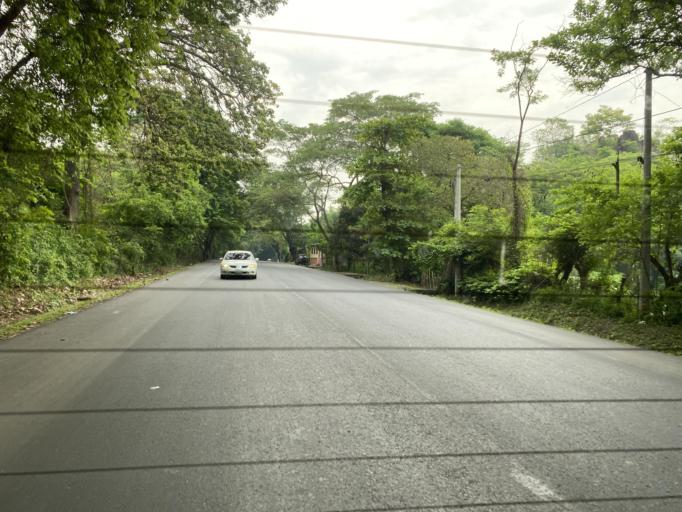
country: SV
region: San Miguel
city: Chirilagua
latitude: 13.3500
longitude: -88.1477
